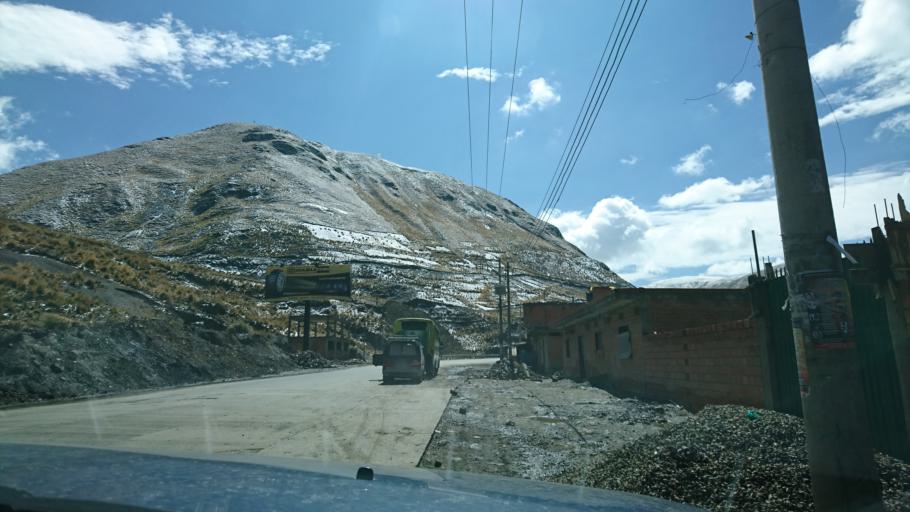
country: BO
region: La Paz
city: La Paz
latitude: -16.4296
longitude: -68.0722
